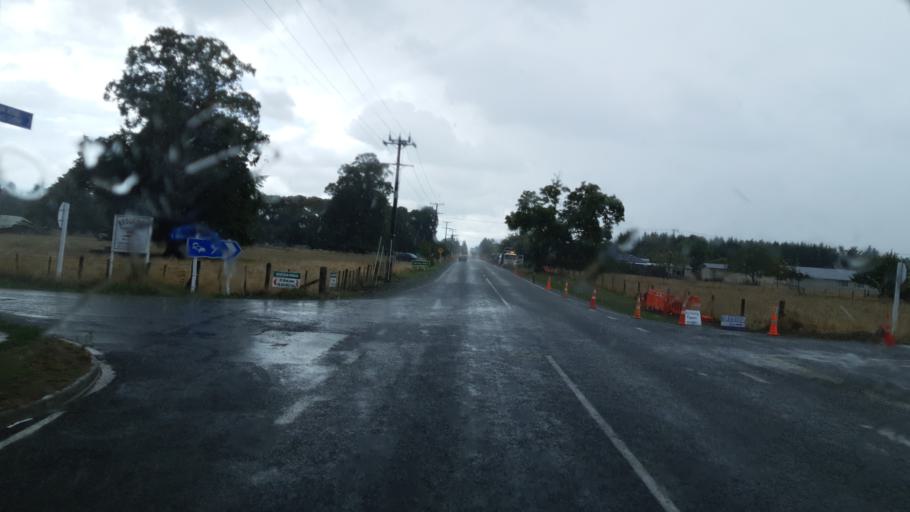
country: NZ
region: Tasman
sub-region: Tasman District
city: Wakefield
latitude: -41.3991
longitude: 173.0596
